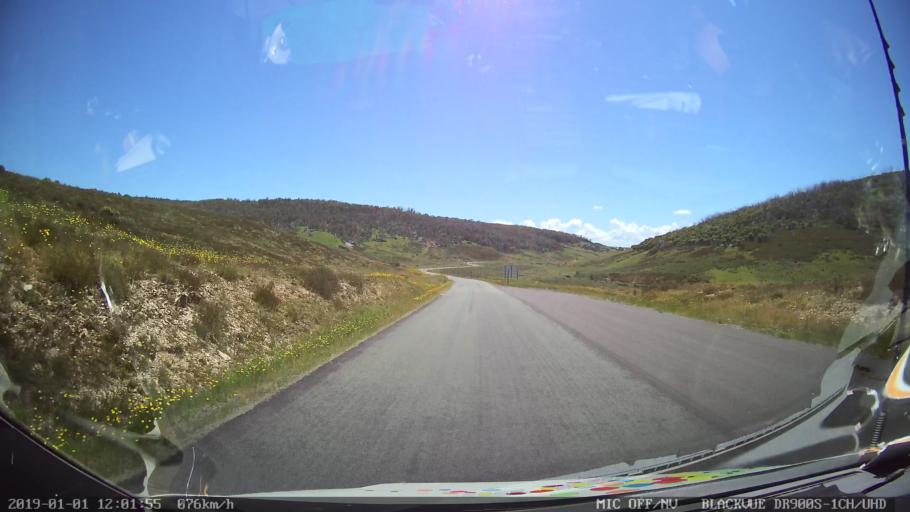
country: AU
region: New South Wales
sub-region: Snowy River
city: Jindabyne
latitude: -35.8767
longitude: 148.4728
